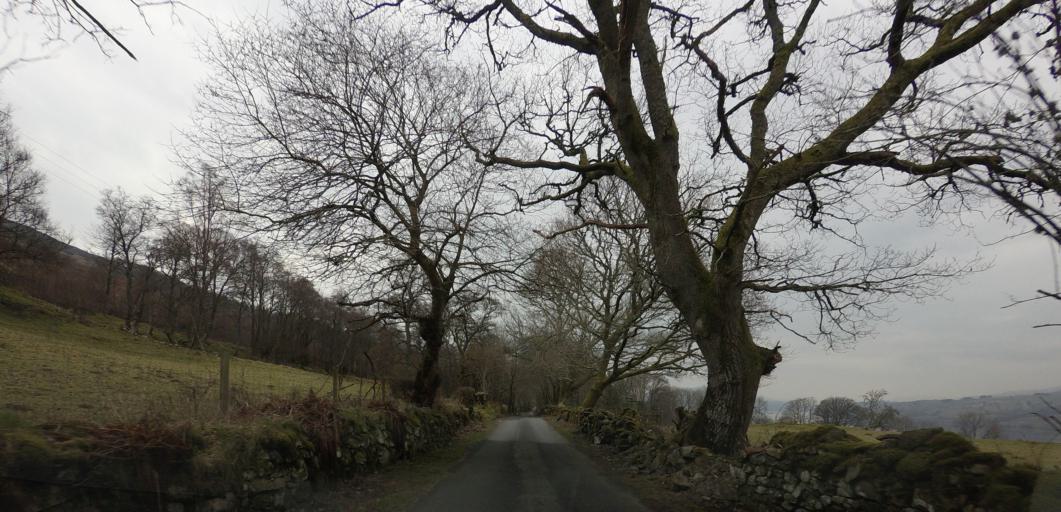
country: GB
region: Scotland
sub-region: Perth and Kinross
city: Comrie
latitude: 56.5389
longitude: -4.1033
